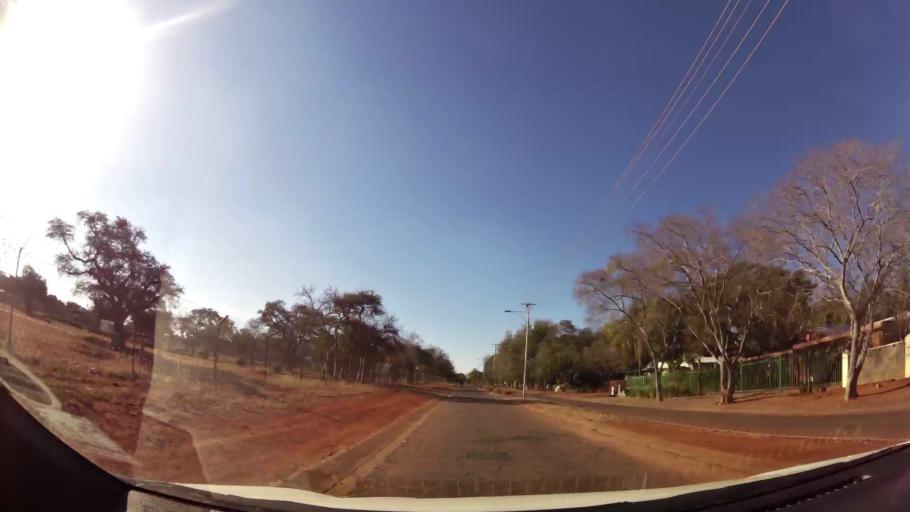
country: ZA
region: Limpopo
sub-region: Waterberg District Municipality
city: Mokopane
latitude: -24.1995
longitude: 29.0095
